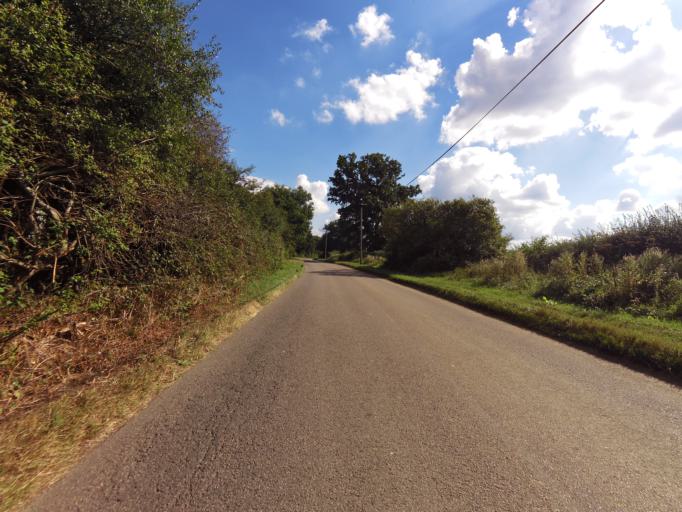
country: GB
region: England
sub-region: Greater London
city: High Barnet
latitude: 51.6642
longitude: -0.2310
